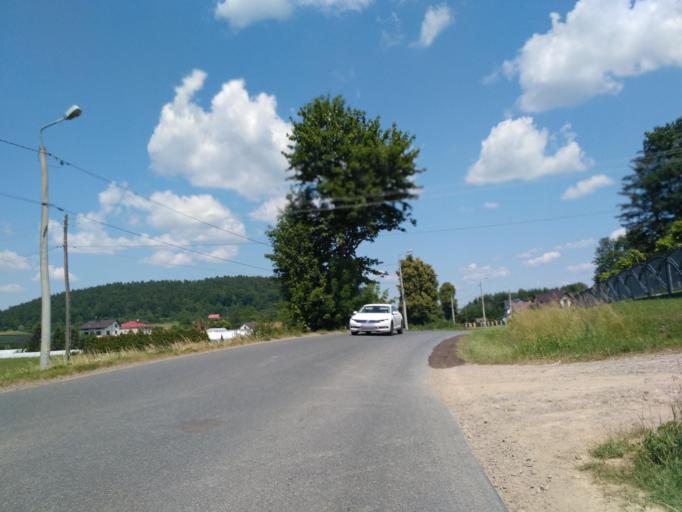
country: PL
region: Subcarpathian Voivodeship
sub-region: Powiat sanocki
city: Niebieszczany
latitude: 49.5433
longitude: 22.1338
